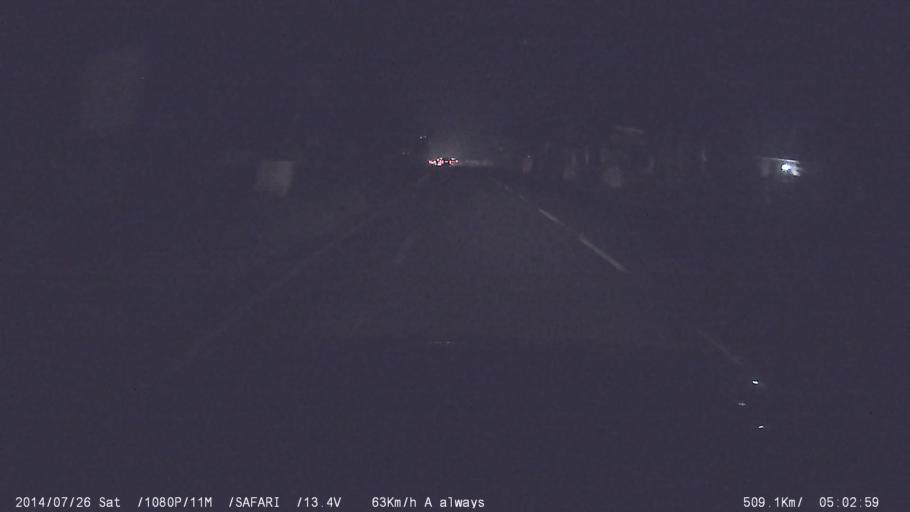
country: IN
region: Kerala
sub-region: Ernakulam
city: Perumbavoor
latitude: 10.1026
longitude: 76.4855
